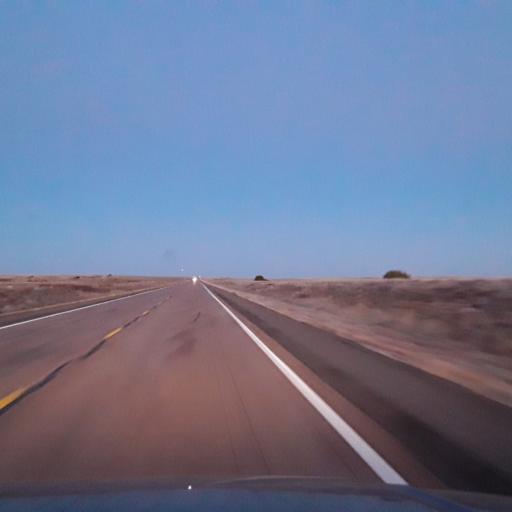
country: US
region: New Mexico
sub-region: Guadalupe County
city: Santa Rosa
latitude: 34.7598
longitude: -104.9909
